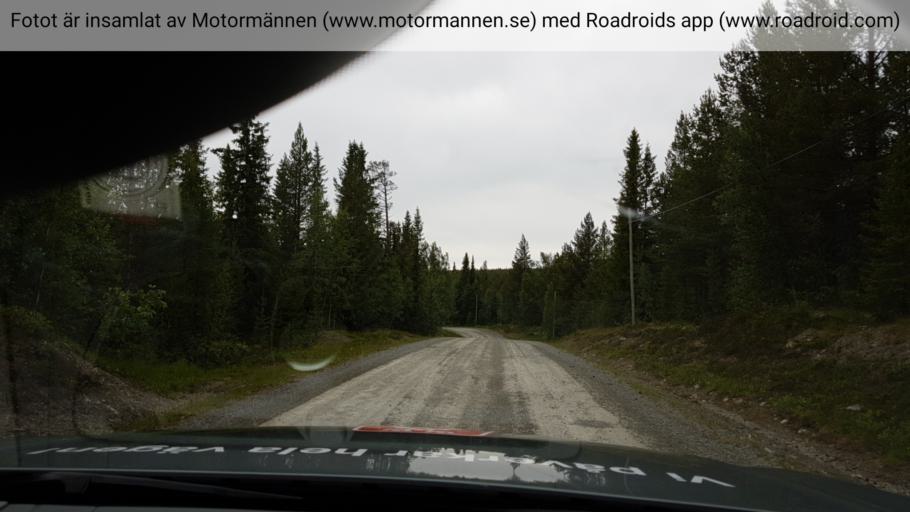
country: SE
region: Jaemtland
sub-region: Are Kommun
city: Jarpen
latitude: 62.8228
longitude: 13.8113
